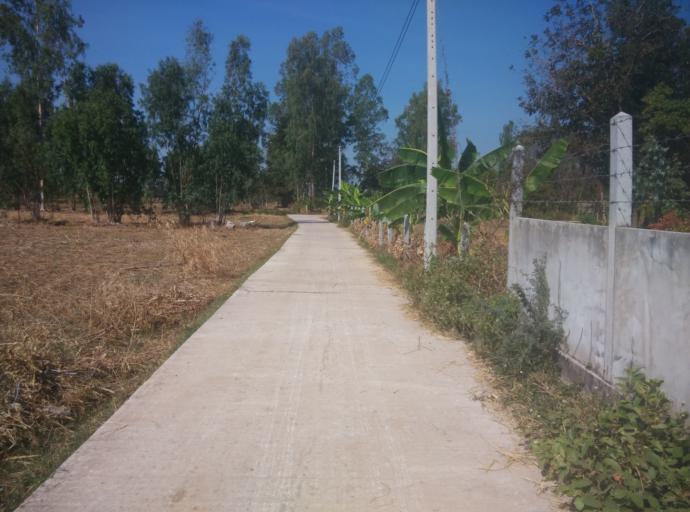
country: TH
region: Sisaket
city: Huai Thap Than
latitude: 15.0505
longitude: 104.0821
